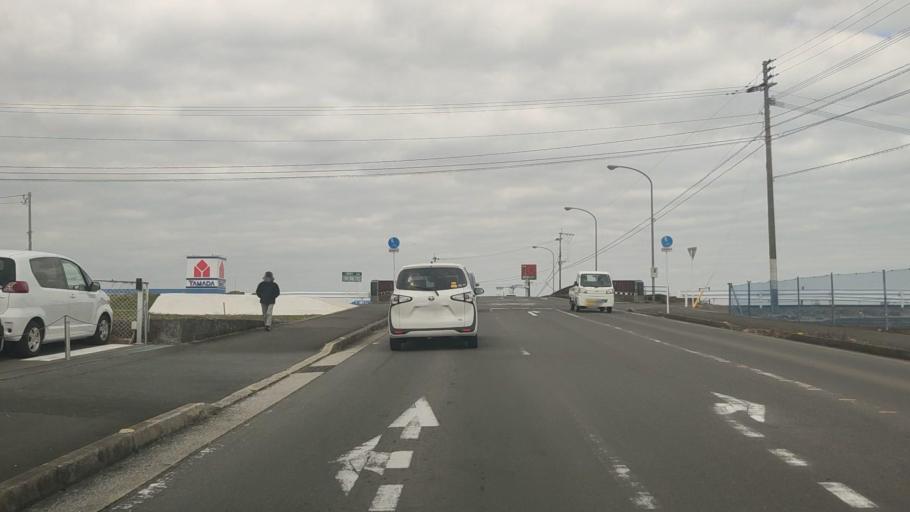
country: JP
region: Nagasaki
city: Shimabara
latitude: 32.8073
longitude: 130.3612
